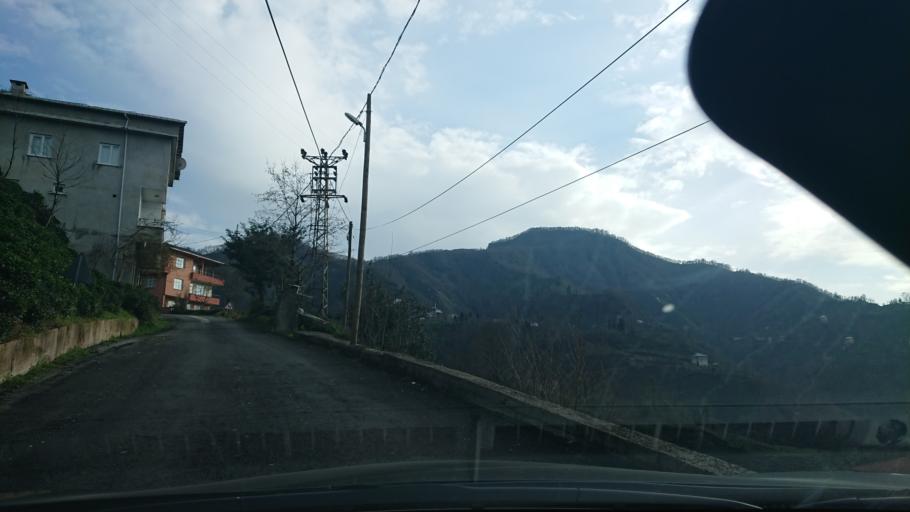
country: TR
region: Rize
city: Rize
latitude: 40.9851
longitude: 40.4919
